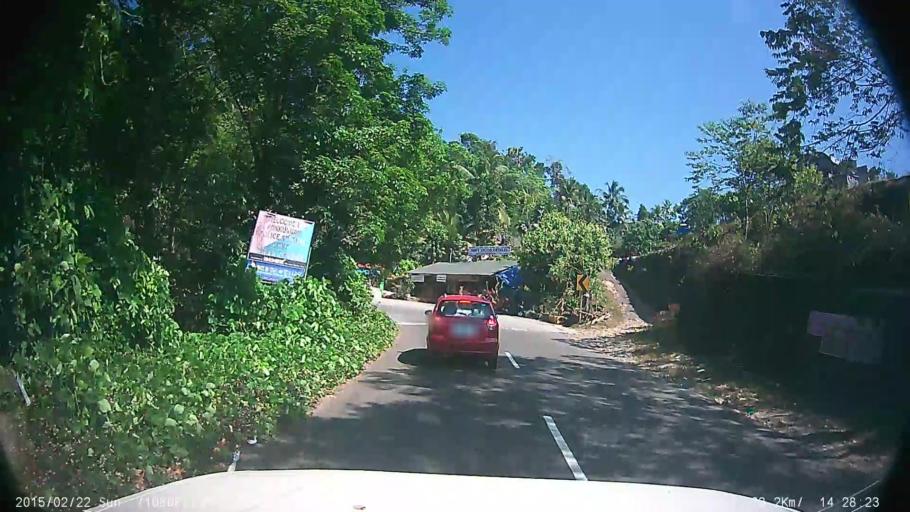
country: IN
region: Kerala
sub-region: Kottayam
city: Erattupetta
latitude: 9.5652
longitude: 76.7405
